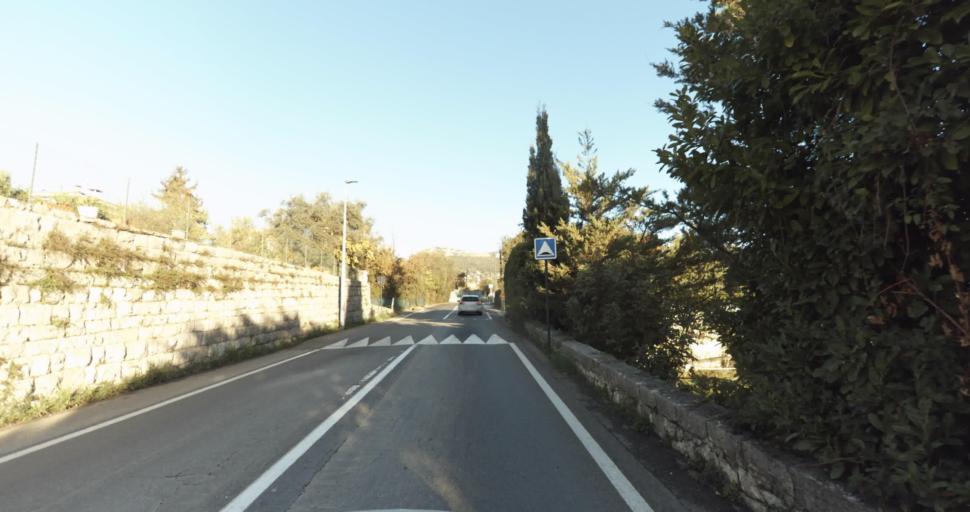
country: FR
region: Provence-Alpes-Cote d'Azur
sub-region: Departement des Alpes-Maritimes
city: Saint-Paul-de-Vence
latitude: 43.7106
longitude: 7.1302
